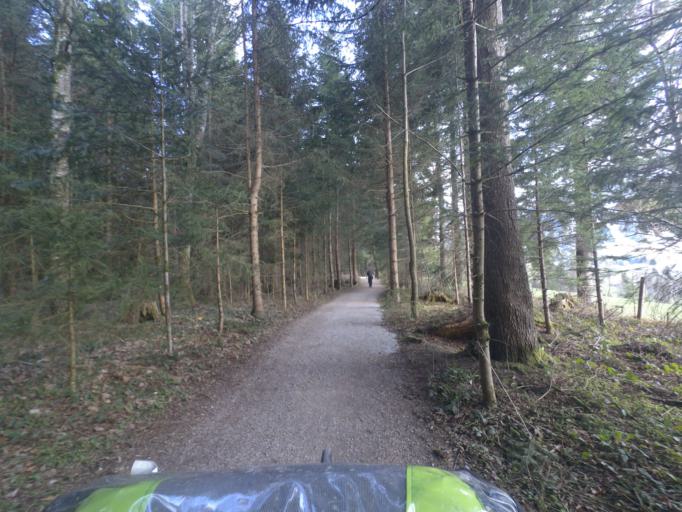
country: AT
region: Salzburg
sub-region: Politischer Bezirk Hallein
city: Abtenau
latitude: 47.5716
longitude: 13.3495
